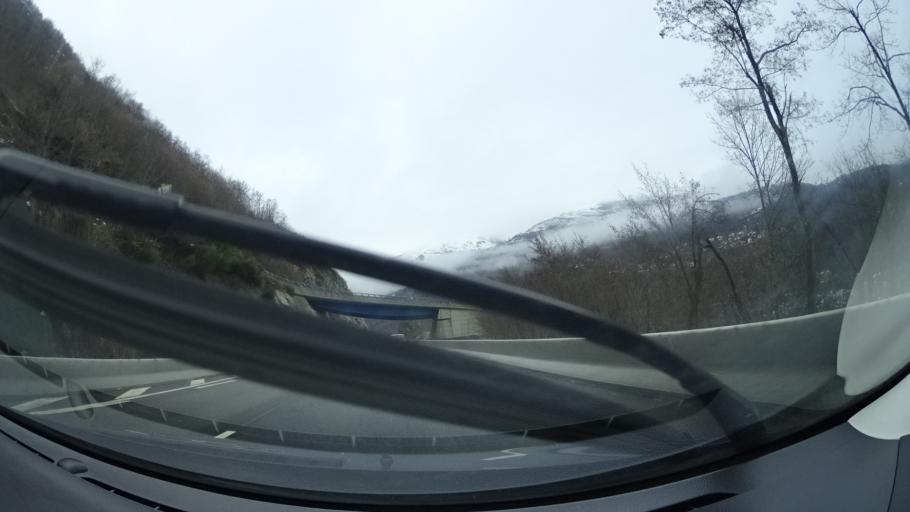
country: FR
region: Midi-Pyrenees
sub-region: Departement de l'Ariege
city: Ax-les-Thermes
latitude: 42.7180
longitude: 1.8342
